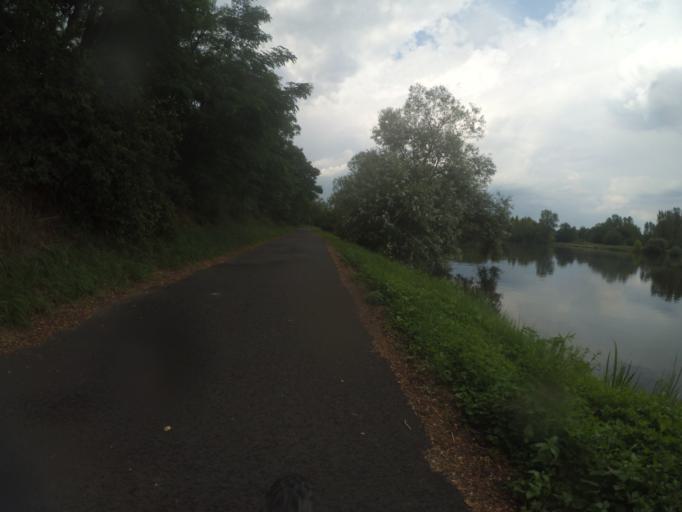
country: CZ
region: Central Bohemia
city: Dolni Berkovice
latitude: 50.3691
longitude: 14.4518
